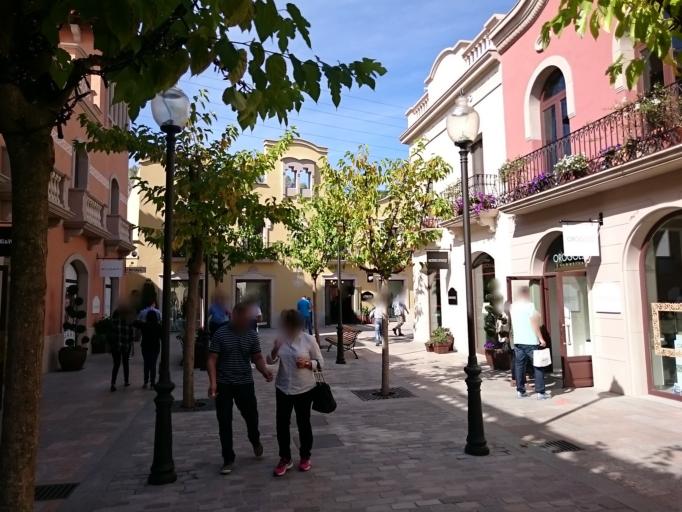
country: ES
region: Catalonia
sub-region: Provincia de Barcelona
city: Cardedeu
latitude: 41.6125
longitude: 2.3449
